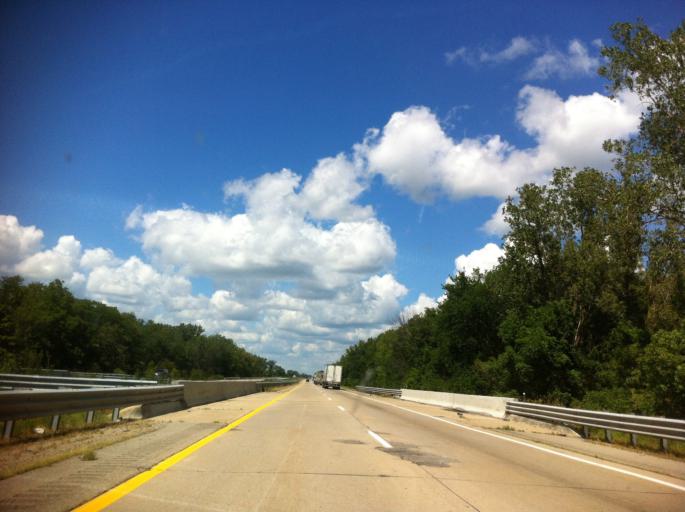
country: US
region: Michigan
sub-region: Monroe County
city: Dundee
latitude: 41.9801
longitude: -83.6783
